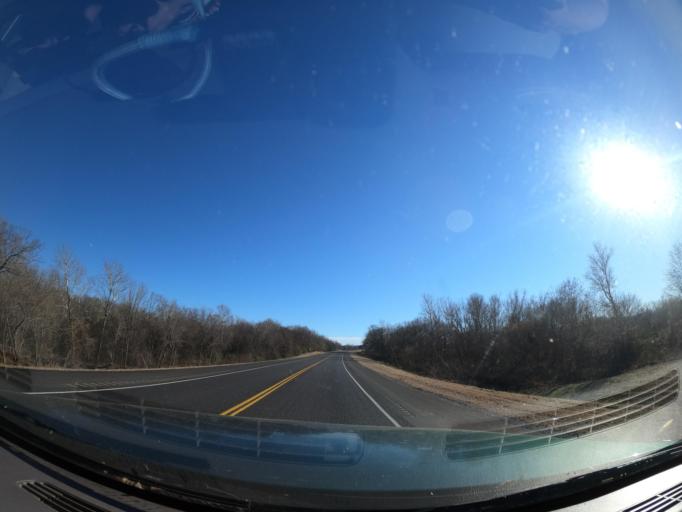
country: US
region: Oklahoma
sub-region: McIntosh County
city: Eufaula
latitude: 35.2653
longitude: -95.5814
